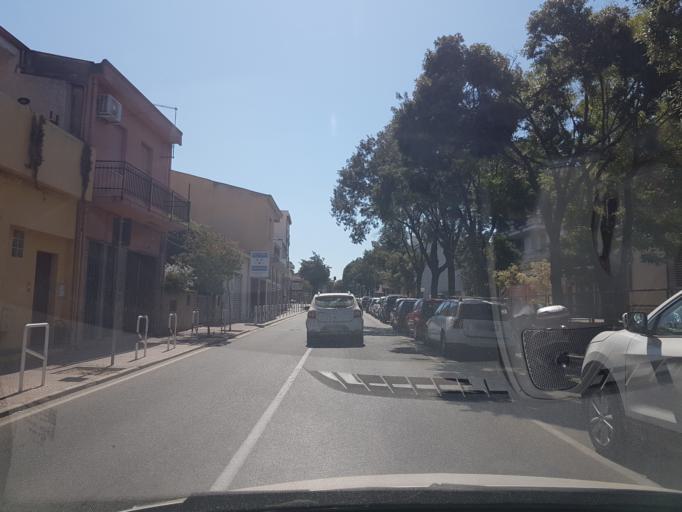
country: IT
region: Sardinia
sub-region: Provincia di Oristano
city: Oristano
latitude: 39.8997
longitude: 8.5928
